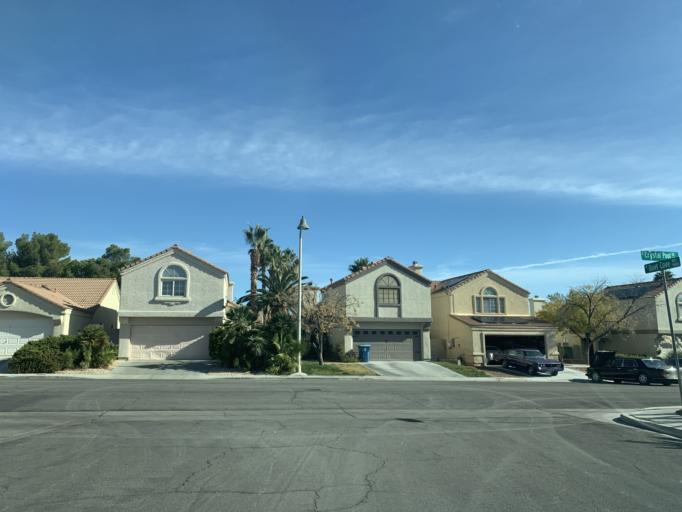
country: US
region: Nevada
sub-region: Clark County
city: Summerlin South
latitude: 36.1321
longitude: -115.2942
